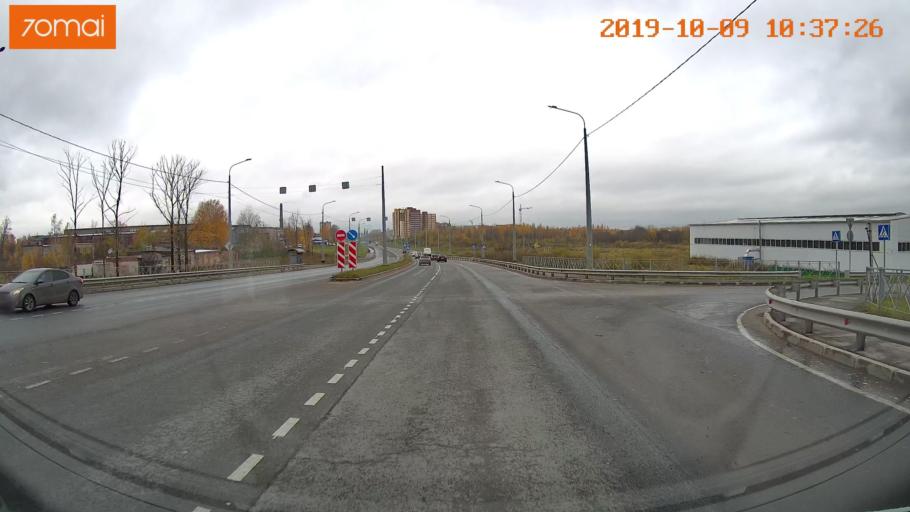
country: RU
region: Vologda
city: Vologda
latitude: 59.2350
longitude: 39.8625
